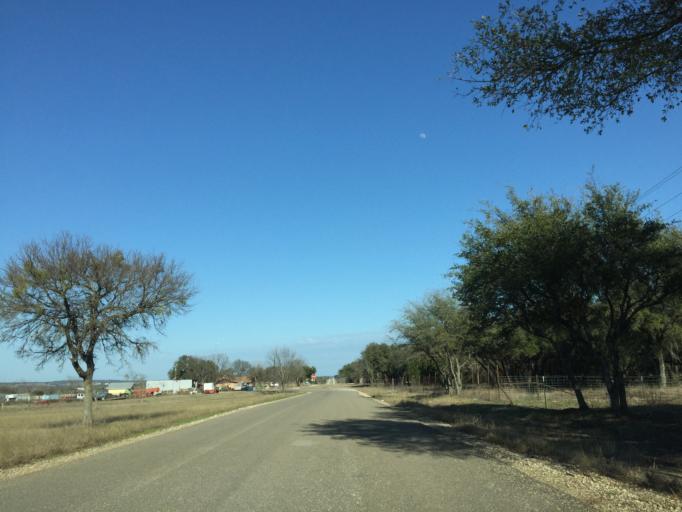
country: US
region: Texas
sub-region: Williamson County
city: Florence
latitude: 30.7643
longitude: -97.8443
